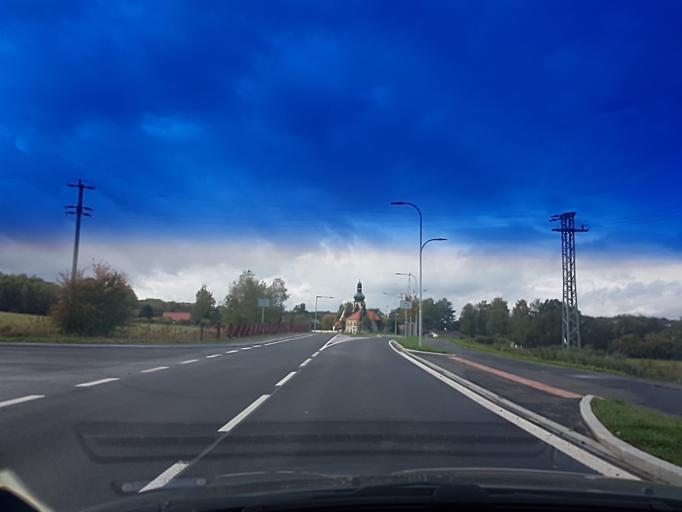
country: DE
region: Bavaria
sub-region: Upper Franconia
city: Schirnding
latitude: 50.0859
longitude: 12.2889
